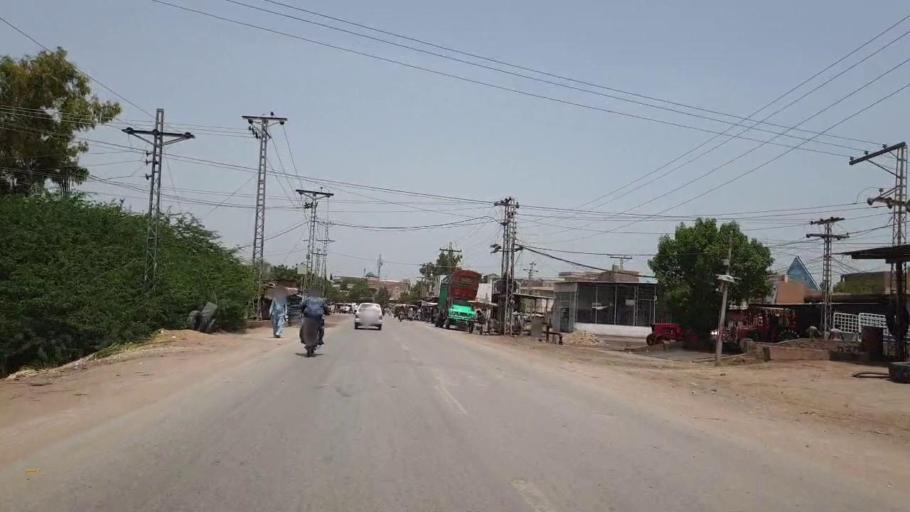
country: PK
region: Sindh
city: Nawabshah
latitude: 26.2510
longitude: 68.4262
